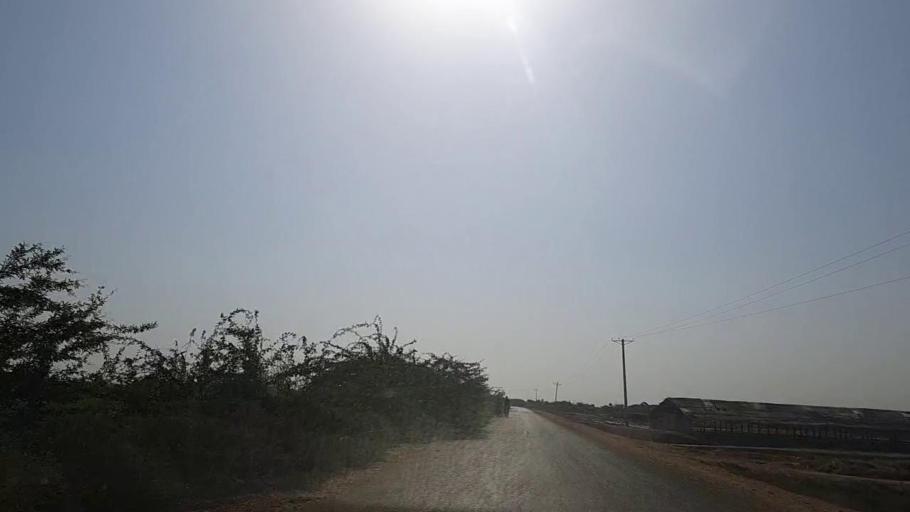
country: PK
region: Sindh
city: Jati
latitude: 24.4589
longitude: 68.2672
